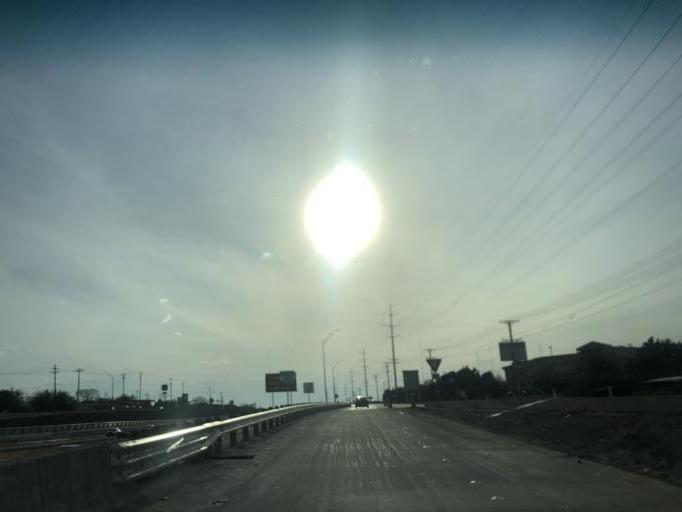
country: US
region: Texas
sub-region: Dallas County
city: Cedar Hill
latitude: 32.6077
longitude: -96.9283
